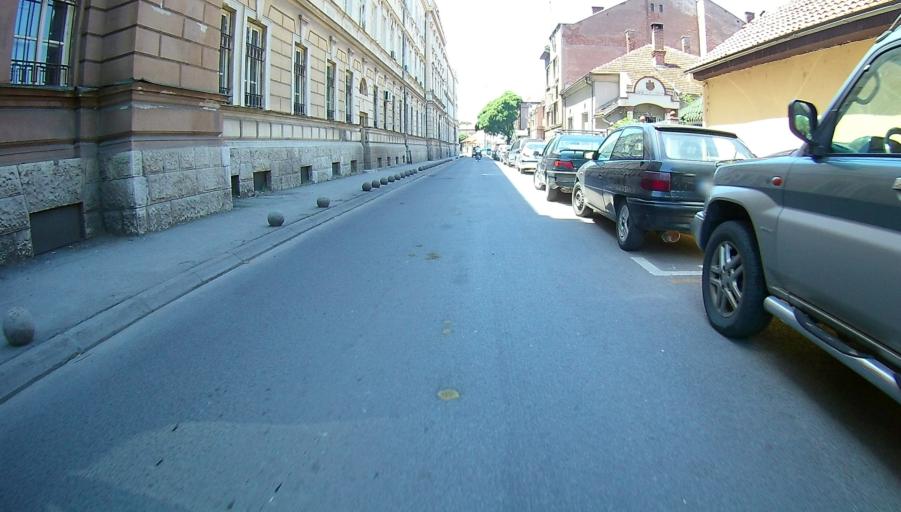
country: RS
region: Central Serbia
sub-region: Nisavski Okrug
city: Nis
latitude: 43.3232
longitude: 21.8935
